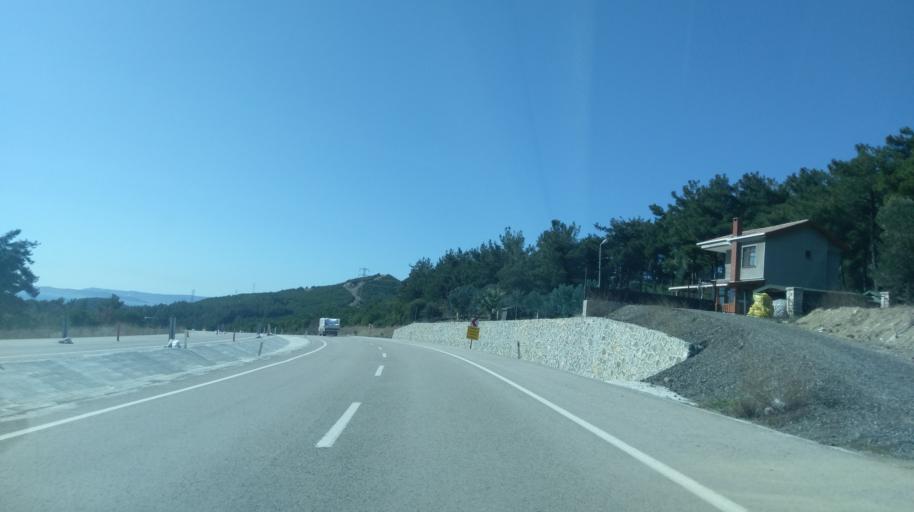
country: TR
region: Canakkale
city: Canakkale
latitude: 40.2559
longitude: 26.4736
